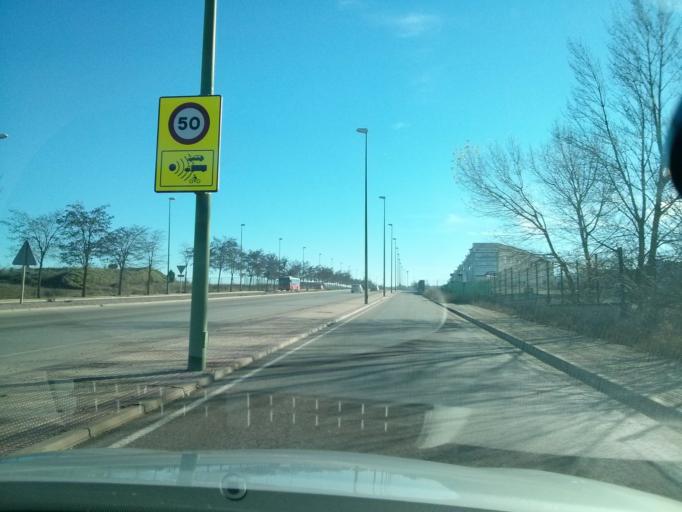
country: ES
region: Castille and Leon
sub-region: Provincia de Burgos
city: Sotragero
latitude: 42.3745
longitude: -3.7221
